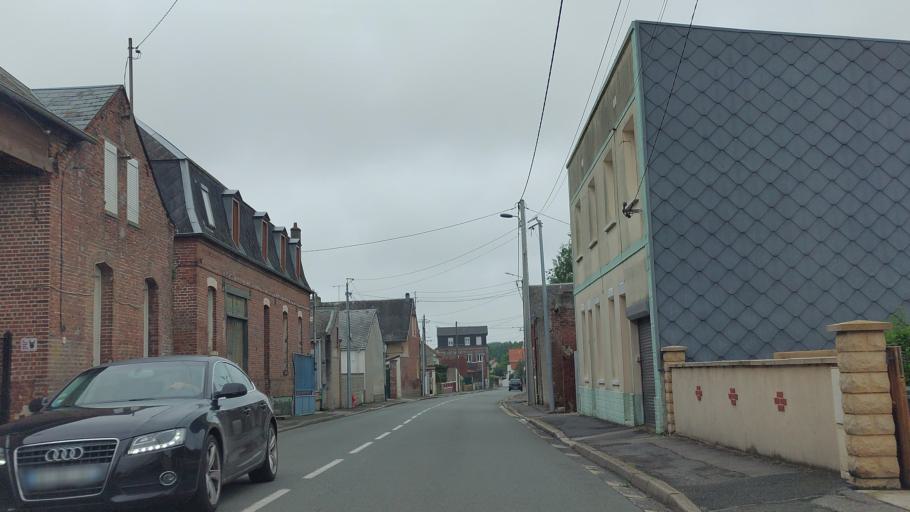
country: FR
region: Picardie
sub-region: Departement de la Somme
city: Bethencourt-sur-Mer
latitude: 50.0852
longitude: 1.4933
